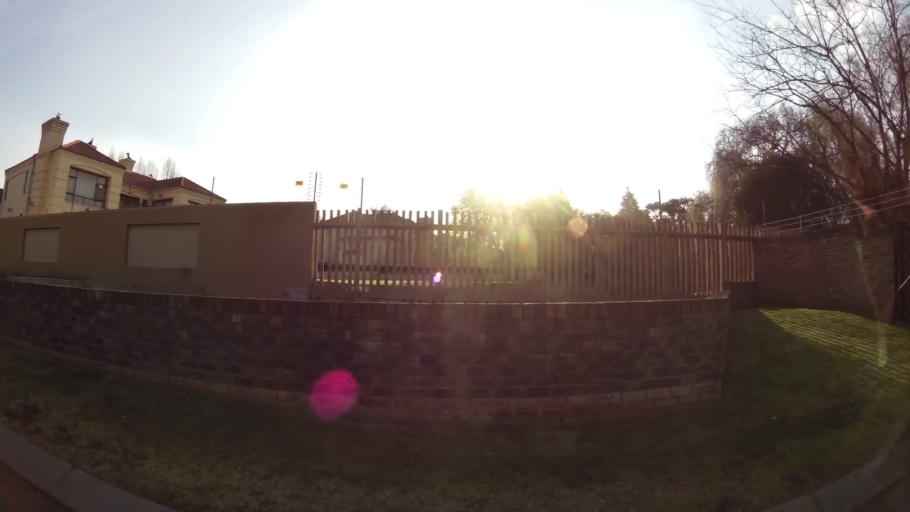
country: ZA
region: Gauteng
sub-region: City of Johannesburg Metropolitan Municipality
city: Modderfontein
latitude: -26.0729
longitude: 28.2233
